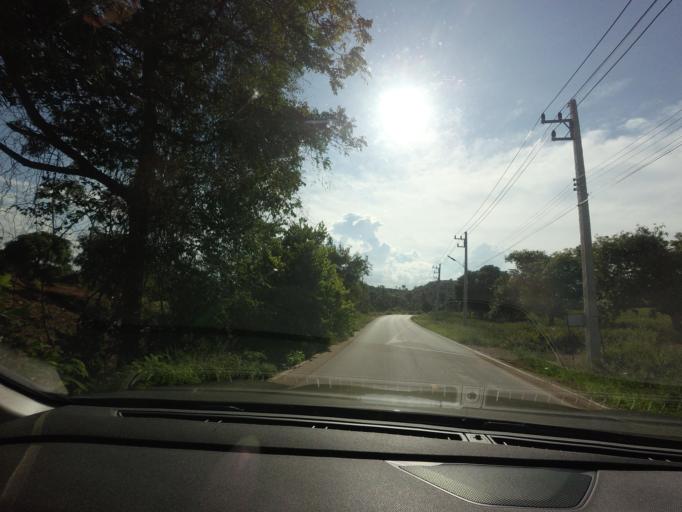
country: TH
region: Prachuap Khiri Khan
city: Pran Buri
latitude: 12.4119
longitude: 99.9705
